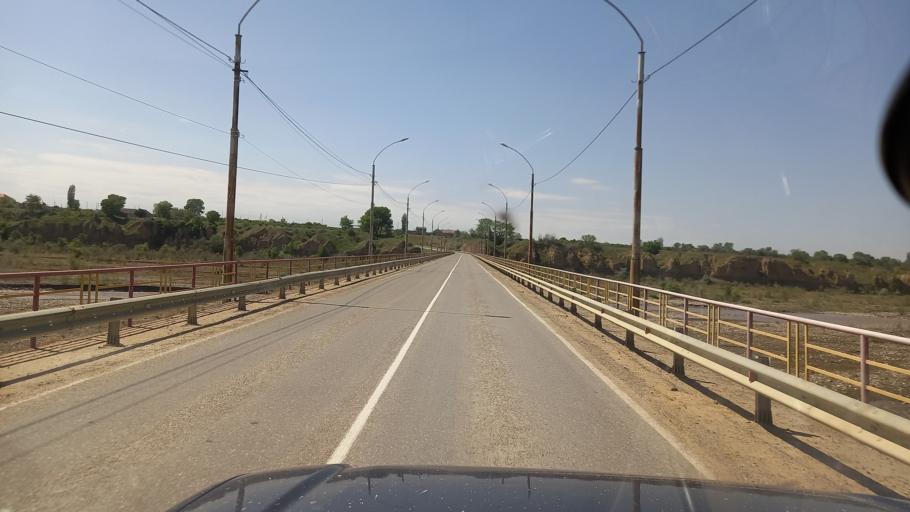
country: RU
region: Dagestan
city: Novaya Maka
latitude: 41.7367
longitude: 48.4488
